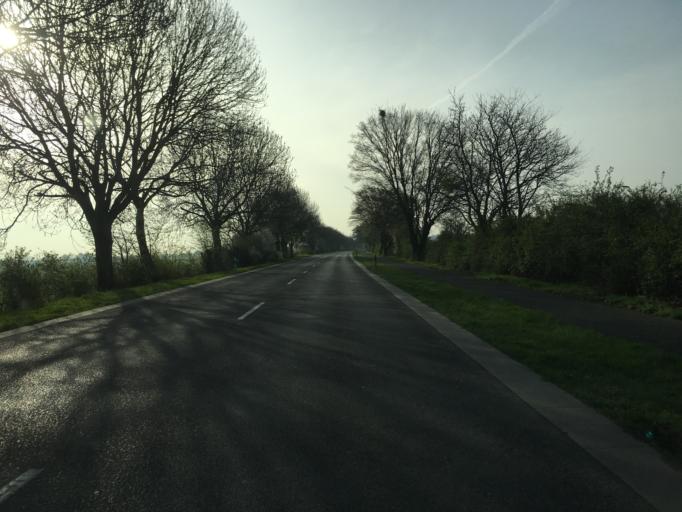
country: DE
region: North Rhine-Westphalia
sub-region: Regierungsbezirk Koln
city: Hurth
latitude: 50.8960
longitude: 6.8477
